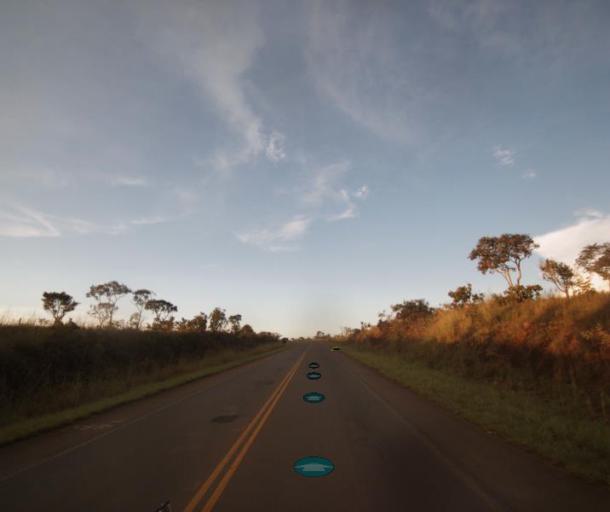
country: BR
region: Goias
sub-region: Abadiania
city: Abadiania
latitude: -16.0829
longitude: -48.8530
